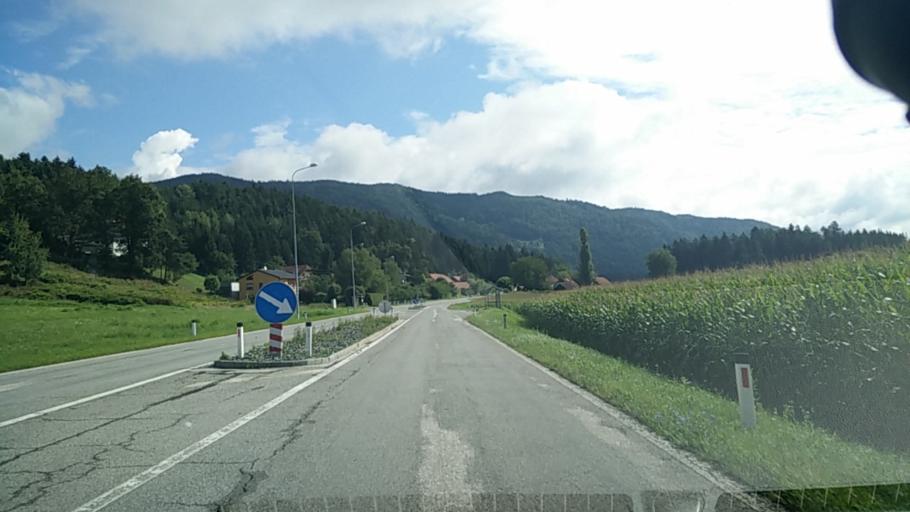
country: AT
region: Carinthia
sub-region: Politischer Bezirk Klagenfurt Land
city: Poggersdorf
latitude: 46.6548
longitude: 14.5258
